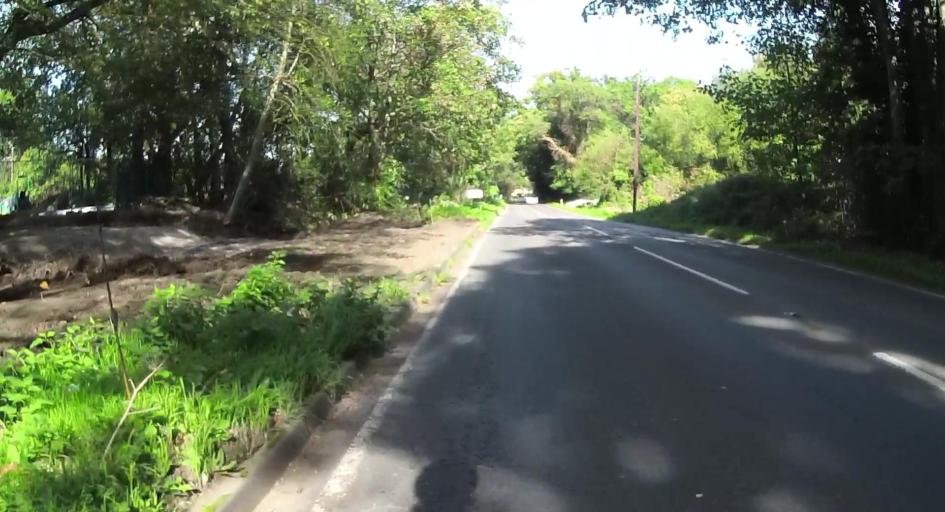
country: GB
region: England
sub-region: Surrey
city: Chertsey
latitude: 51.3843
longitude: -0.5257
